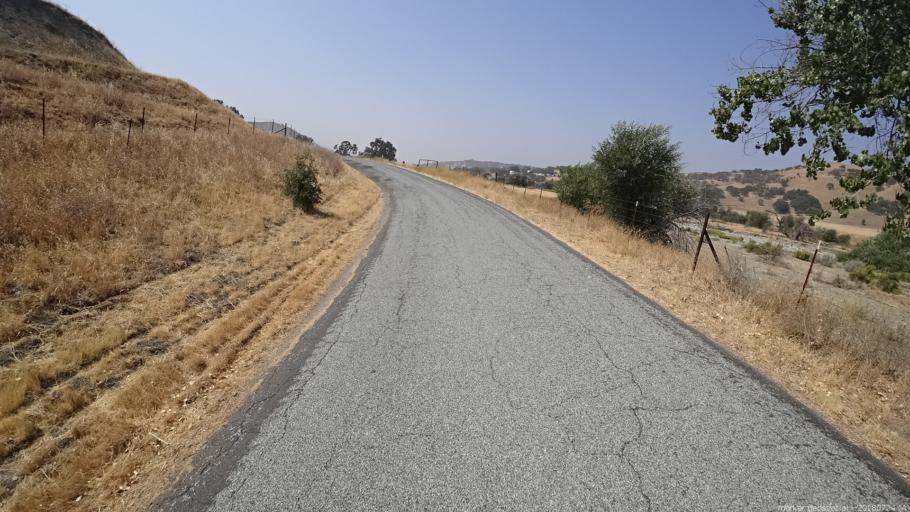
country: US
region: California
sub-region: San Luis Obispo County
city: San Miguel
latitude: 35.9413
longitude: -120.6732
